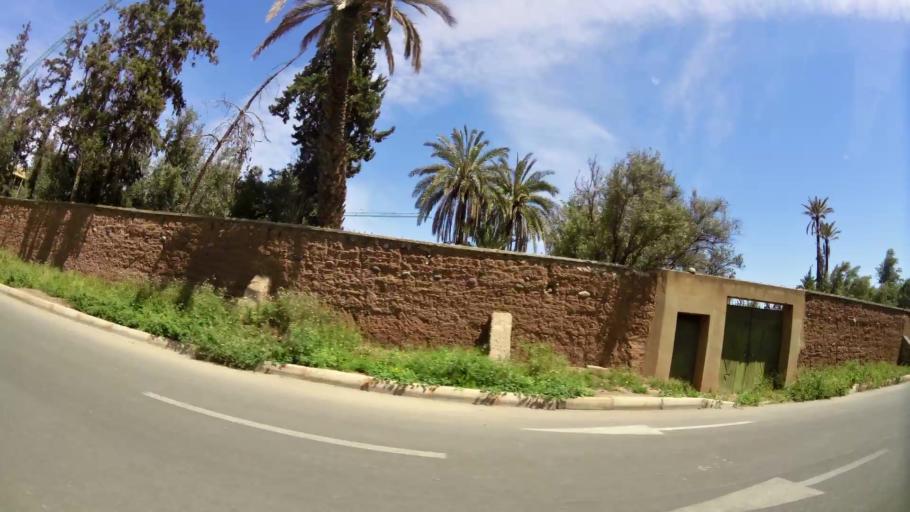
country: MA
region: Marrakech-Tensift-Al Haouz
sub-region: Marrakech
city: Marrakesh
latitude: 31.6423
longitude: -8.0605
